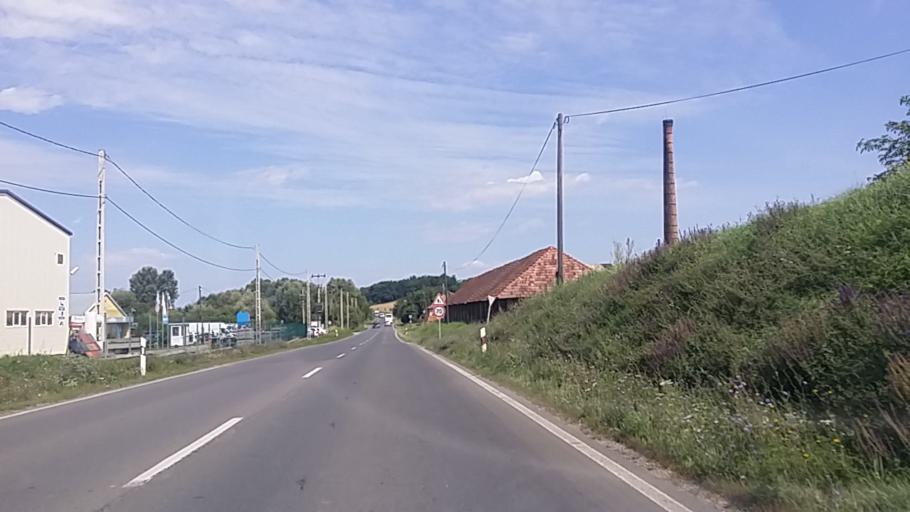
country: HU
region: Baranya
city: Sasd
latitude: 46.2427
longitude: 18.1207
